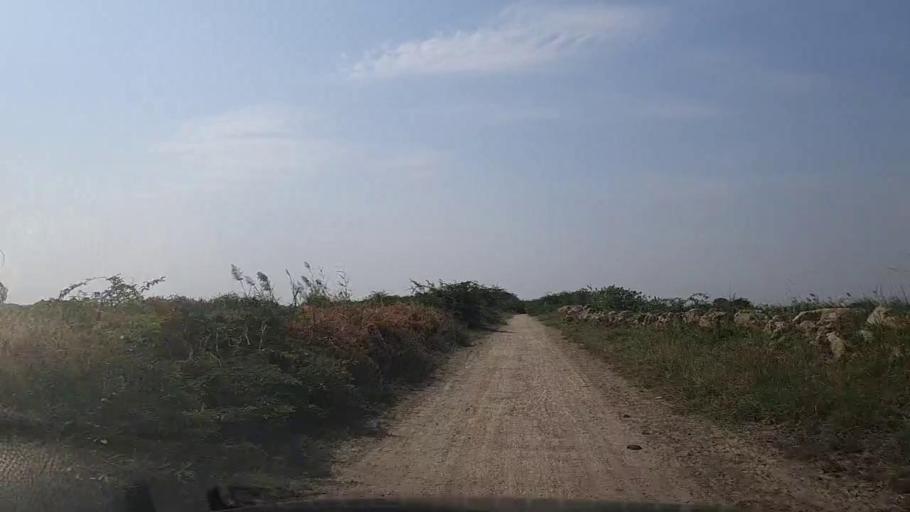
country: PK
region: Sindh
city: Thatta
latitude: 24.7713
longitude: 67.8164
